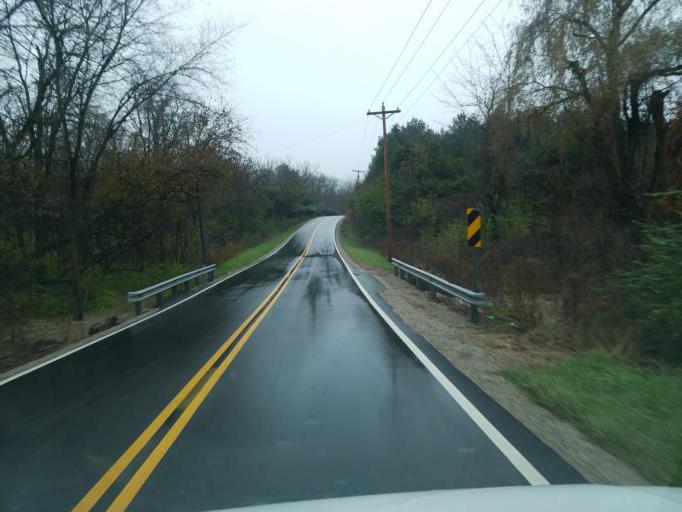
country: US
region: Ohio
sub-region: Delaware County
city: Ashley
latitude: 40.3408
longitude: -82.9195
